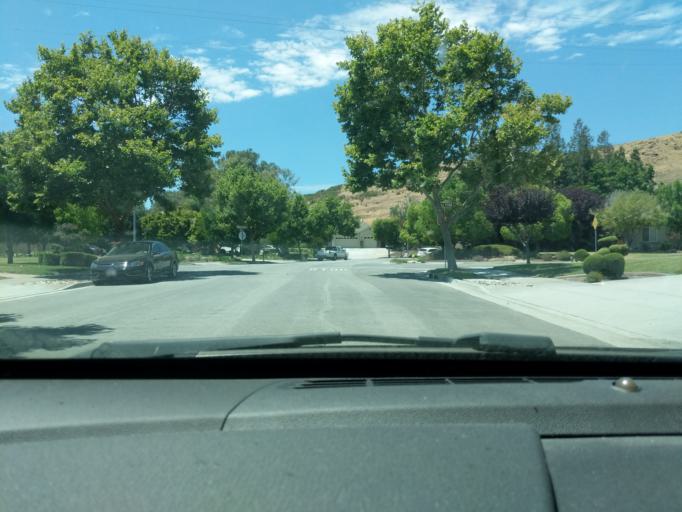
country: US
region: California
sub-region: Santa Clara County
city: Morgan Hill
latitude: 37.1369
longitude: -121.6738
